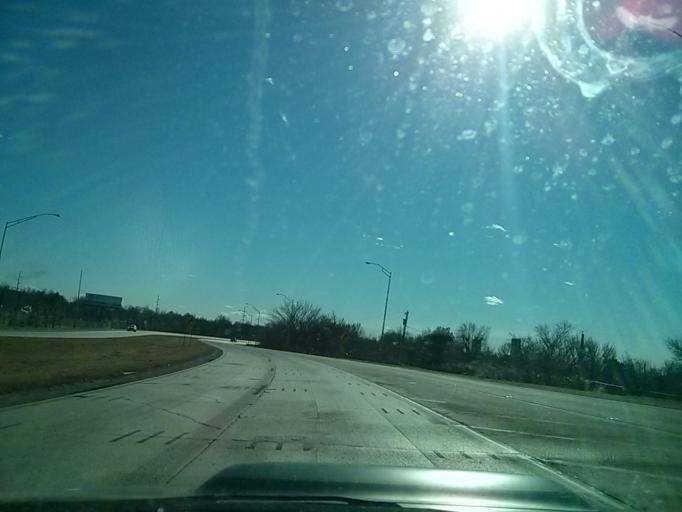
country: US
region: Oklahoma
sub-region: Tulsa County
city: Tulsa
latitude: 36.1885
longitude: -95.9602
